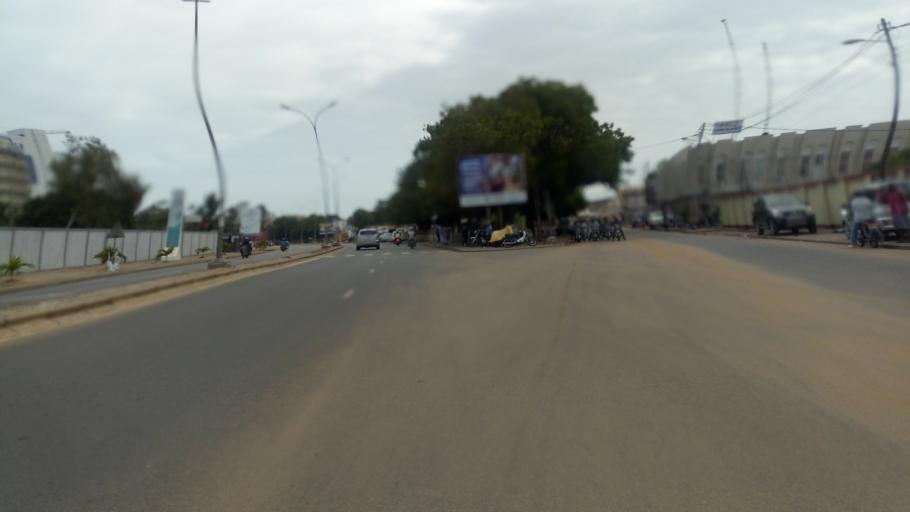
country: TG
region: Maritime
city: Lome
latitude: 6.1286
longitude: 1.2103
